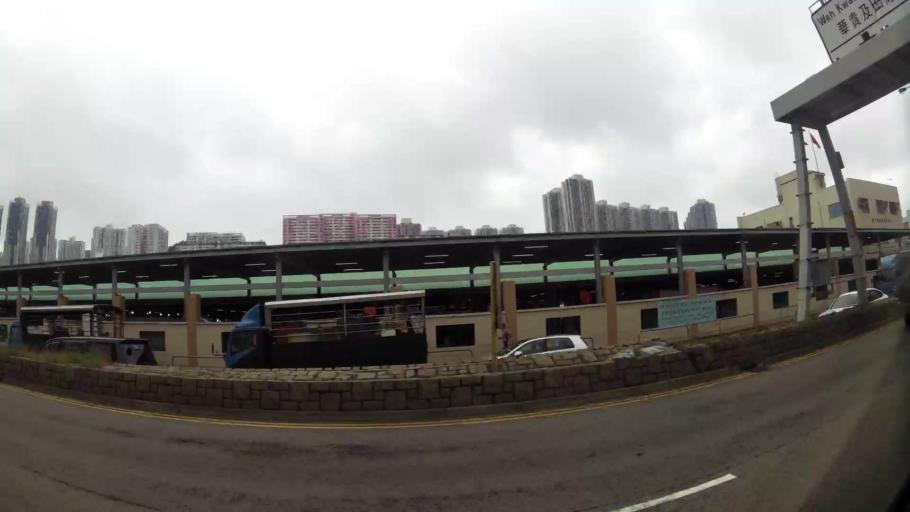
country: HK
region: Central and Western
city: Central
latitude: 22.2484
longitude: 114.1505
